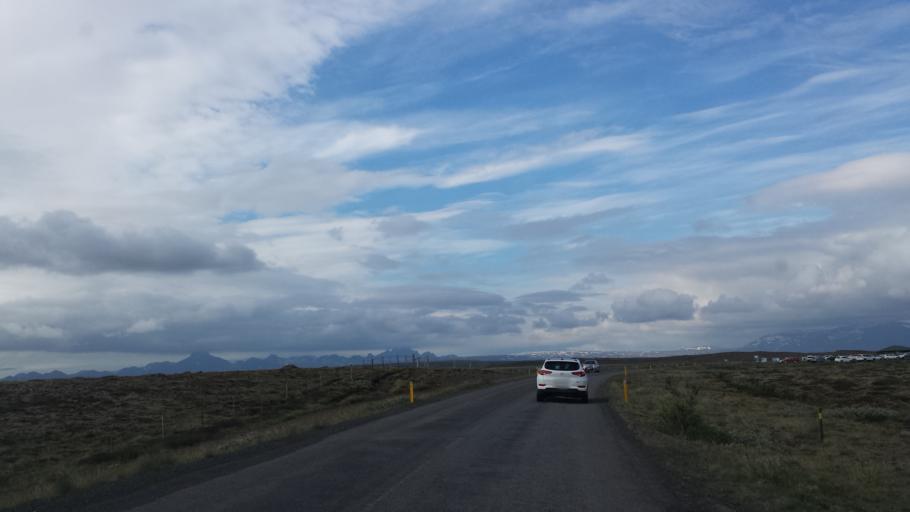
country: IS
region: South
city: Vestmannaeyjar
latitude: 64.3233
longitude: -20.1341
